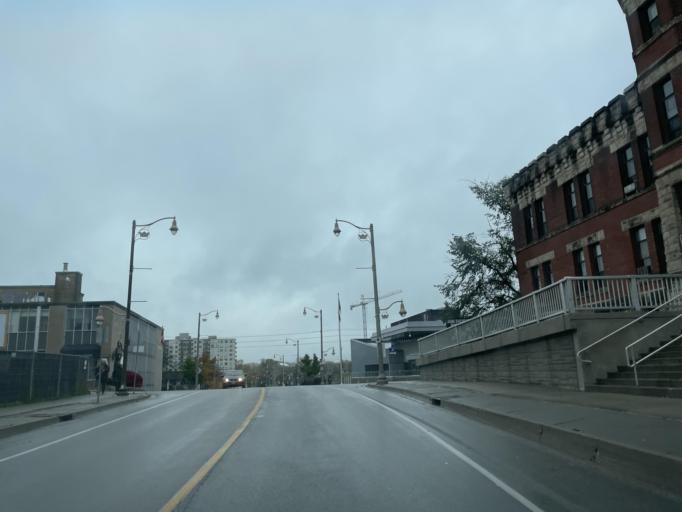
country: CA
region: Ontario
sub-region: Wellington County
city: Guelph
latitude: 43.5437
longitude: -80.2468
